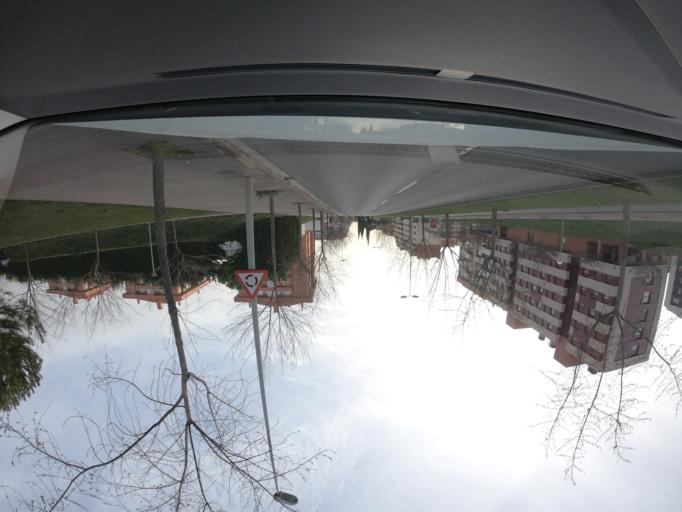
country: ES
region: La Rioja
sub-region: Provincia de La Rioja
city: Logrono
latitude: 42.4530
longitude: -2.4581
